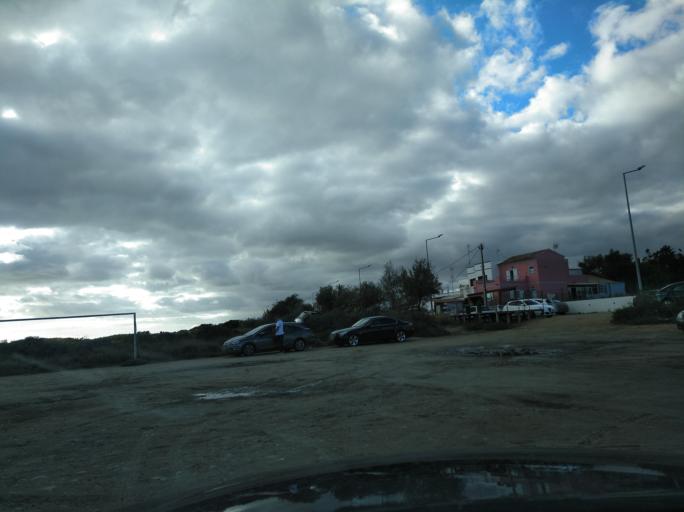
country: PT
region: Faro
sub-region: Tavira
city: Luz
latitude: 37.0719
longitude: -7.7157
